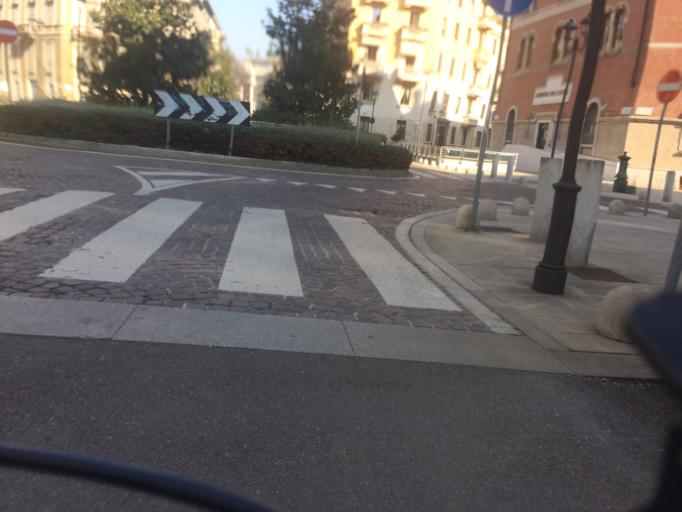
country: IT
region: Lombardy
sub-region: Citta metropolitana di Milano
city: Milano
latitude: 45.4758
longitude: 9.1693
